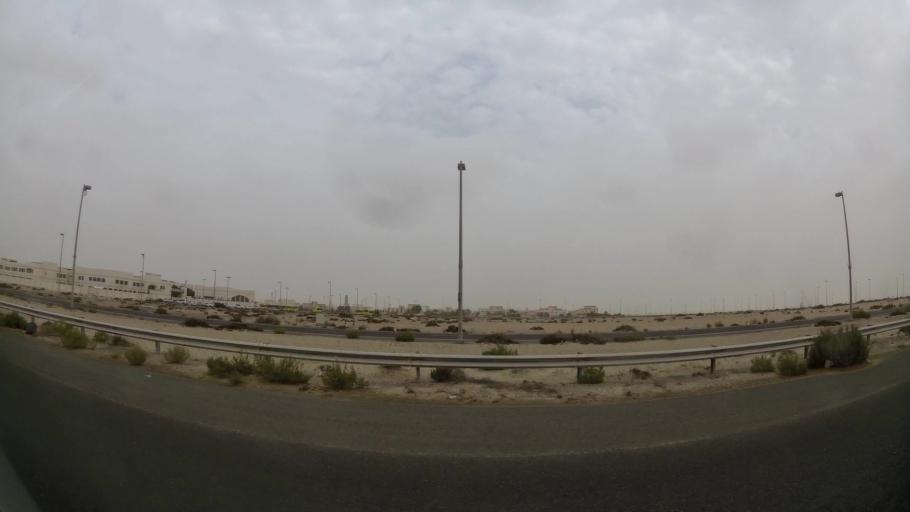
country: AE
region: Abu Dhabi
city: Abu Dhabi
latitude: 24.3899
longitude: 54.7375
